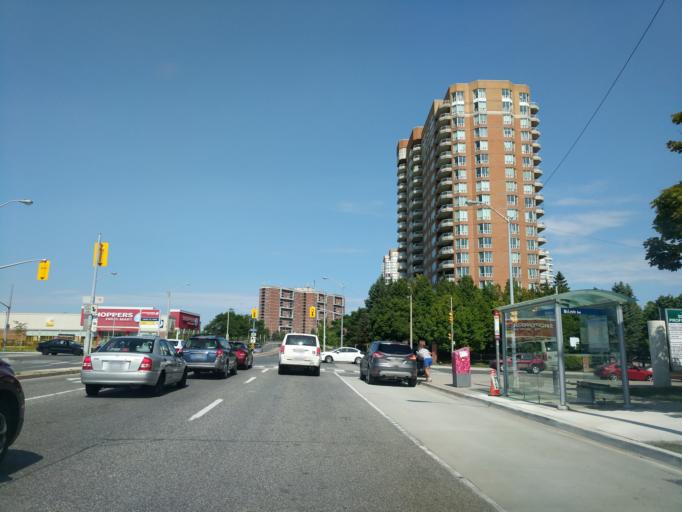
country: CA
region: Ontario
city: Scarborough
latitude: 43.8090
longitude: -79.2211
